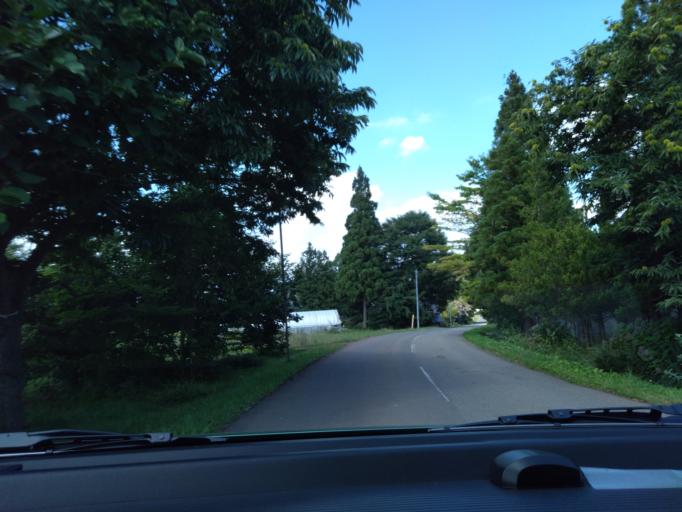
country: JP
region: Iwate
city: Shizukuishi
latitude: 39.6814
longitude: 140.9591
